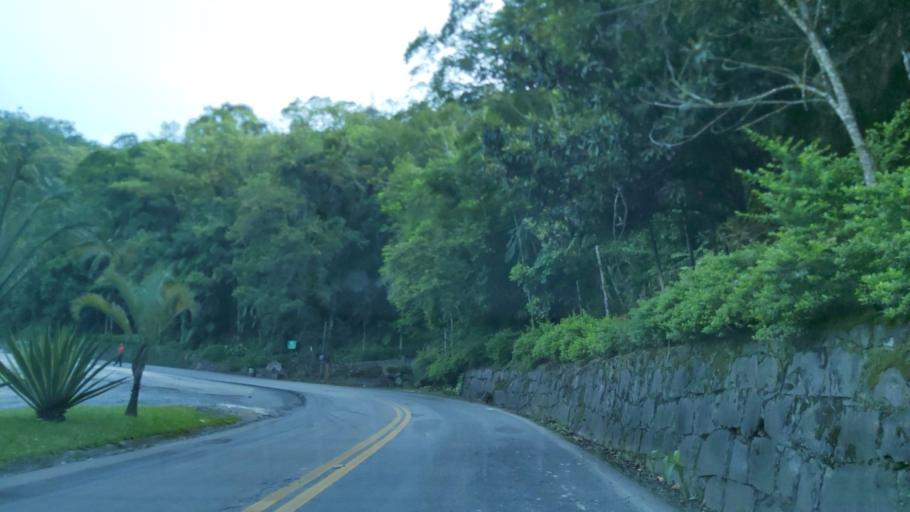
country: BR
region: Sao Paulo
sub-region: Miracatu
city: Miracatu
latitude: -24.0595
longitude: -47.5740
